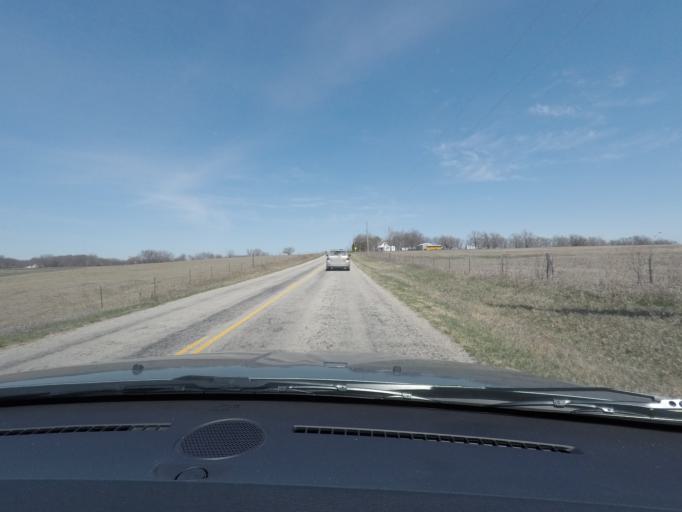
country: US
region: Kansas
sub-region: Lyon County
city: Emporia
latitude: 38.5835
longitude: -96.1699
